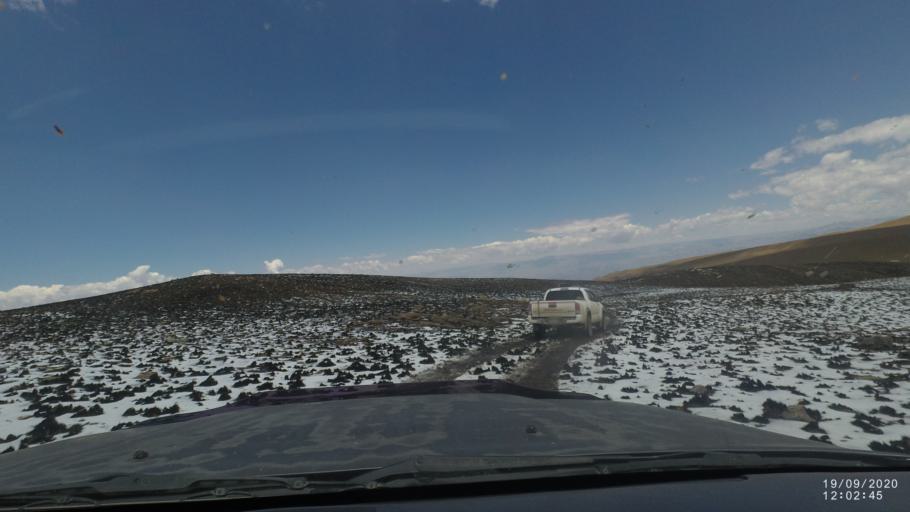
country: BO
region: Cochabamba
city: Cochabamba
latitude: -17.2979
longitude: -66.1050
